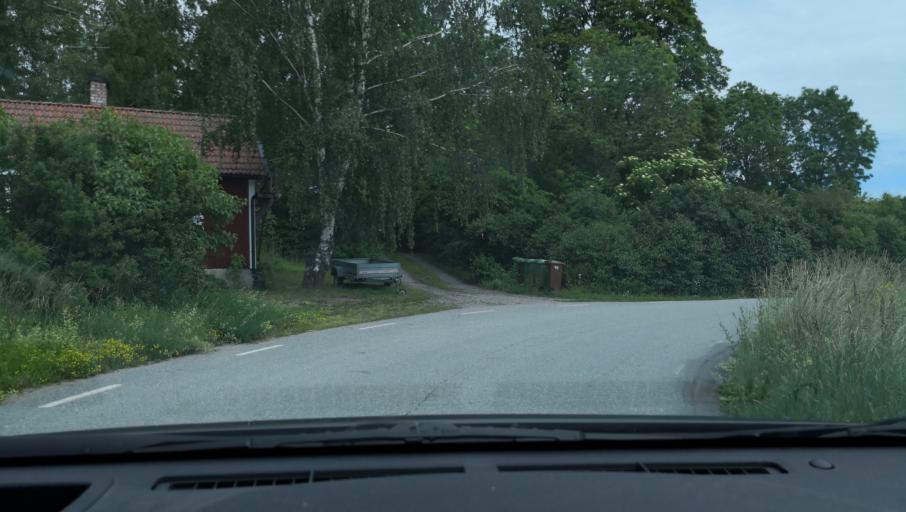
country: SE
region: Uppsala
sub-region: Habo Kommun
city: Balsta
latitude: 59.6932
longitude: 17.4516
